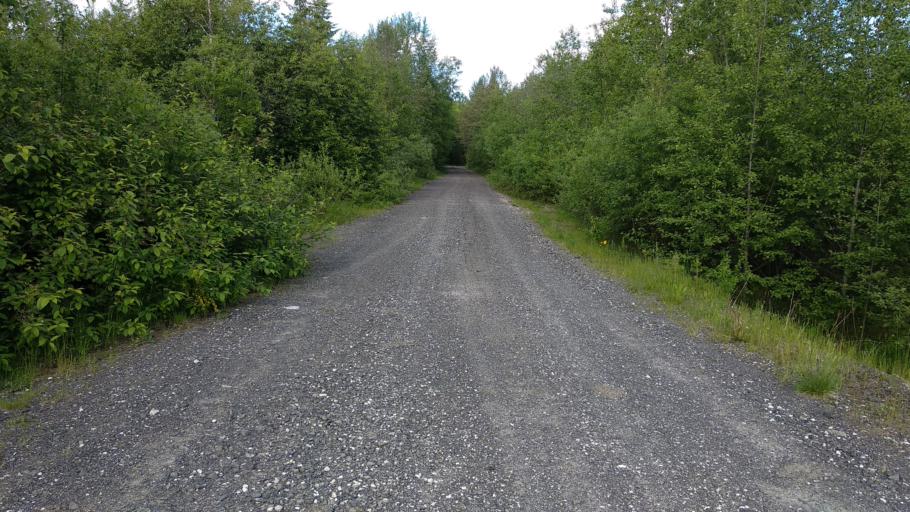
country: RU
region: Sverdlovsk
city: Karpinsk
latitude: 59.7655
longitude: 59.9151
